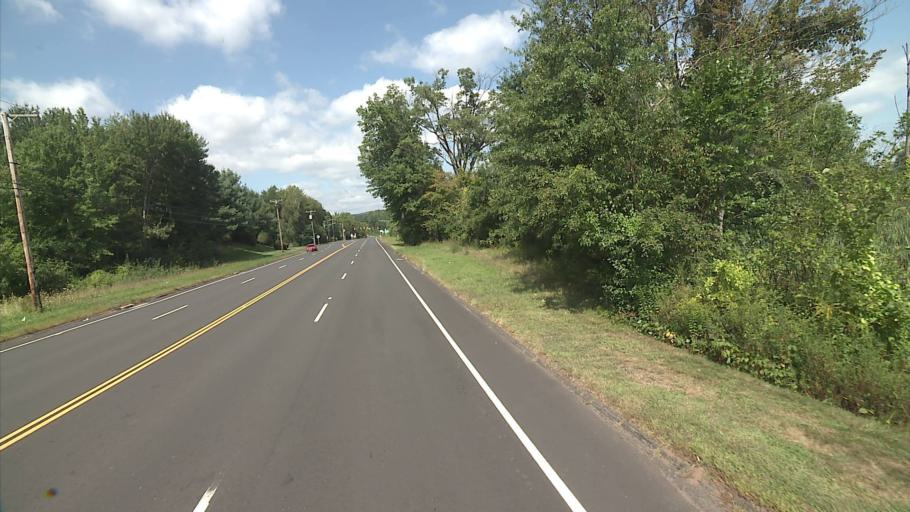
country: US
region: Connecticut
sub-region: Hartford County
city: West Hartford
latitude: 41.8050
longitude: -72.7476
